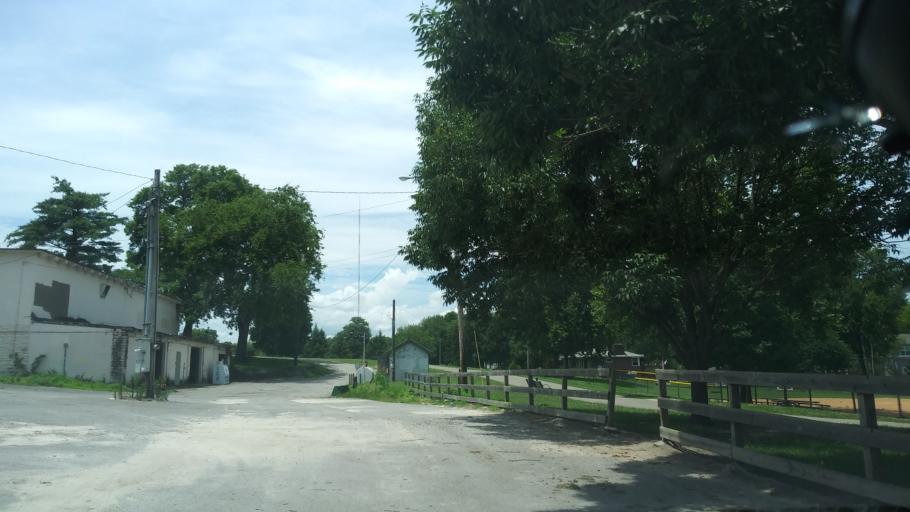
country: US
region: Tennessee
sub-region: Davidson County
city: Belle Meade
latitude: 36.1421
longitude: -86.8443
